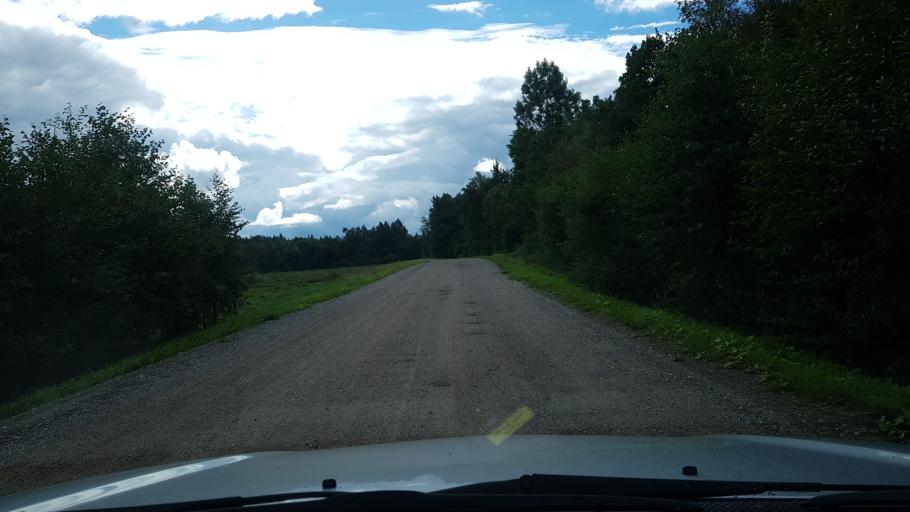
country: EE
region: Harju
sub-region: Rae vald
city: Vaida
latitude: 59.2654
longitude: 25.0488
